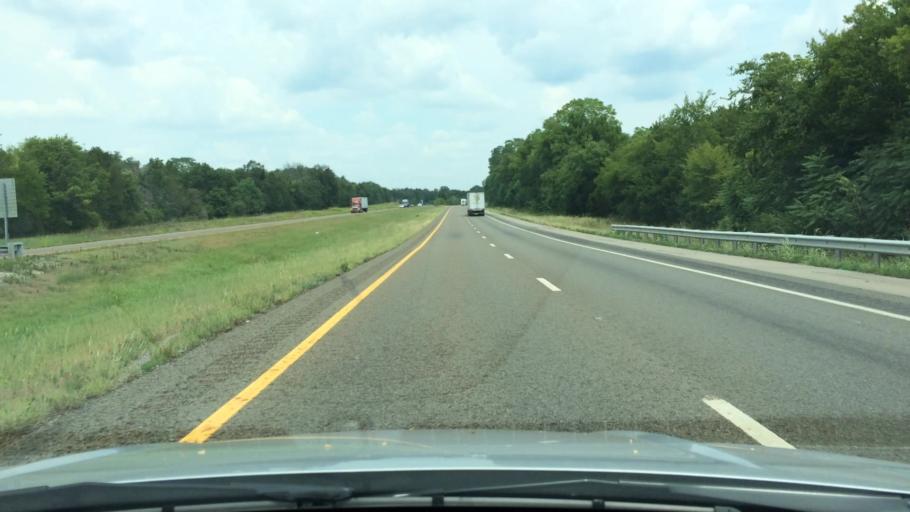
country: US
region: Tennessee
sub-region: Maury County
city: Columbia
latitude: 35.5436
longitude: -86.9060
